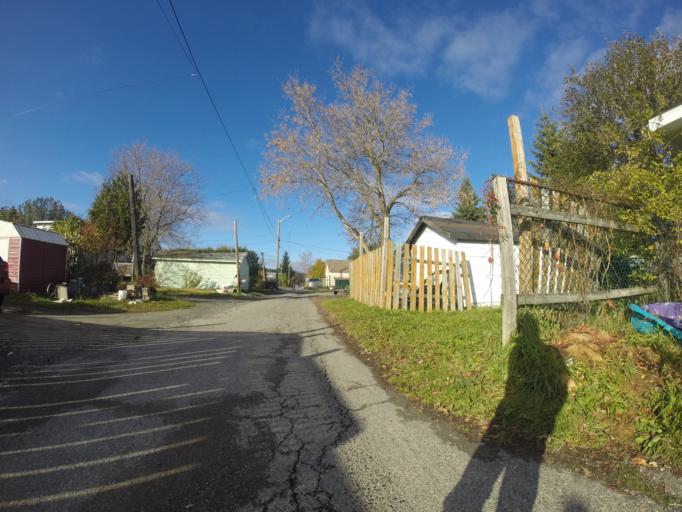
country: CA
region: Ontario
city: Greater Sudbury
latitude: 46.5033
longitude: -81.0064
